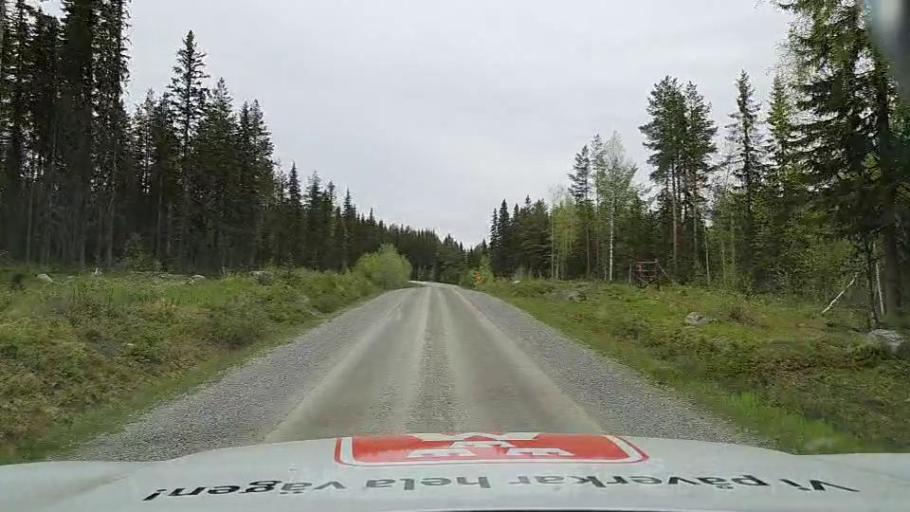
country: SE
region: Jaemtland
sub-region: OEstersunds Kommun
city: Brunflo
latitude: 62.6503
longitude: 14.9255
